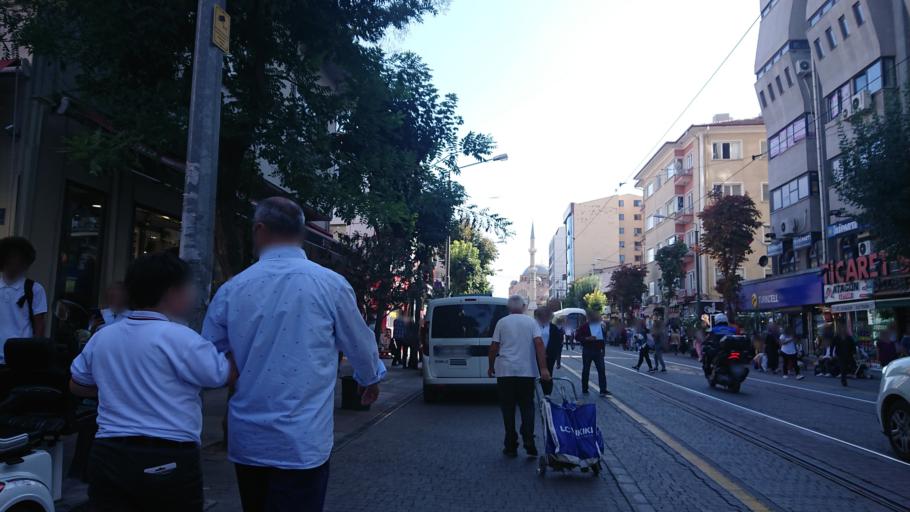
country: TR
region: Eskisehir
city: Eskisehir
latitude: 39.7737
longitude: 30.5176
